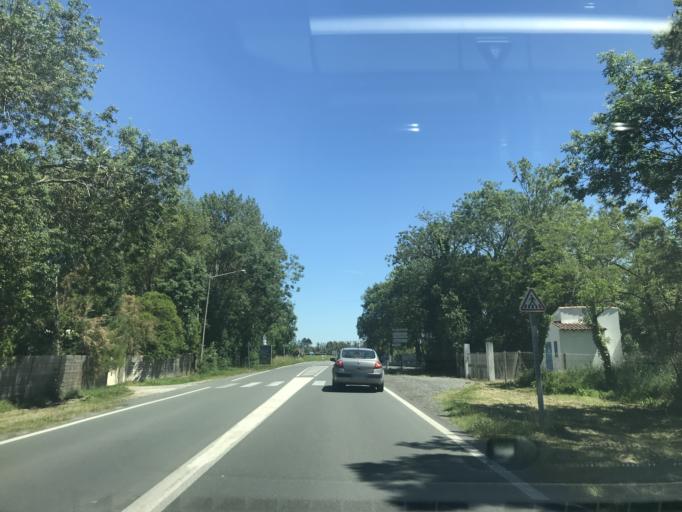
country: FR
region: Poitou-Charentes
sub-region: Departement de la Charente-Maritime
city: Meschers-sur-Gironde
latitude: 45.5631
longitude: -0.9467
